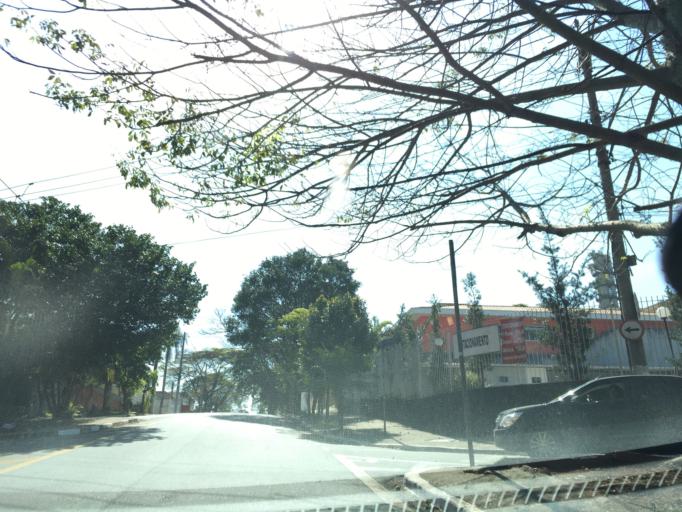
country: BR
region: Sao Paulo
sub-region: Sao Paulo
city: Sao Paulo
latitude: -23.5371
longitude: -46.7129
